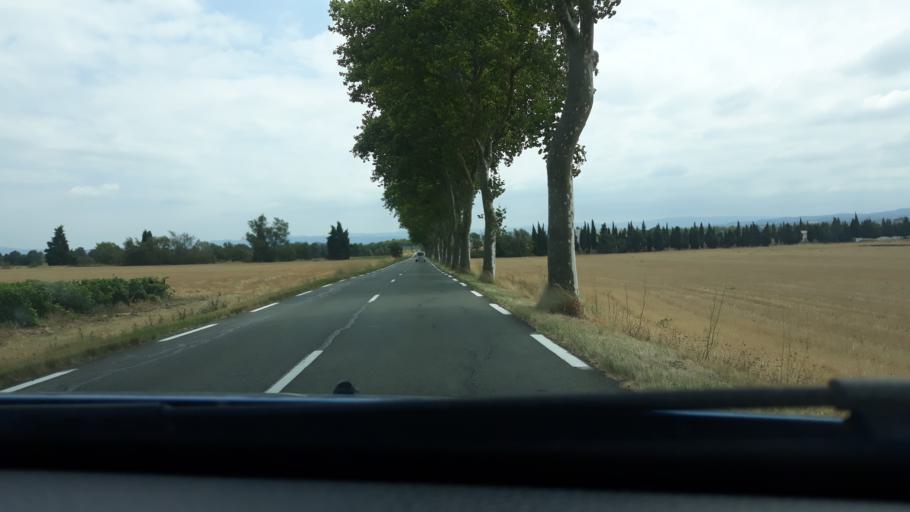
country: FR
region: Languedoc-Roussillon
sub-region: Departement de l'Aude
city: Pezens
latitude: 43.2689
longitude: 2.2387
